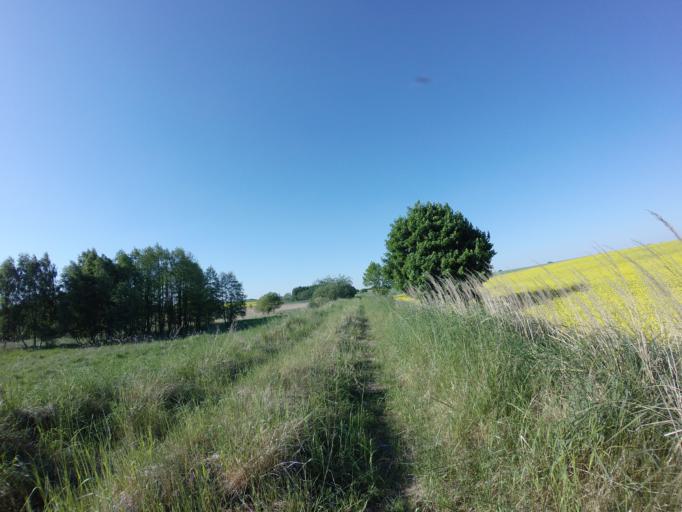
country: PL
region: West Pomeranian Voivodeship
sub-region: Powiat choszczenski
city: Choszczno
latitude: 53.1422
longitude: 15.3697
